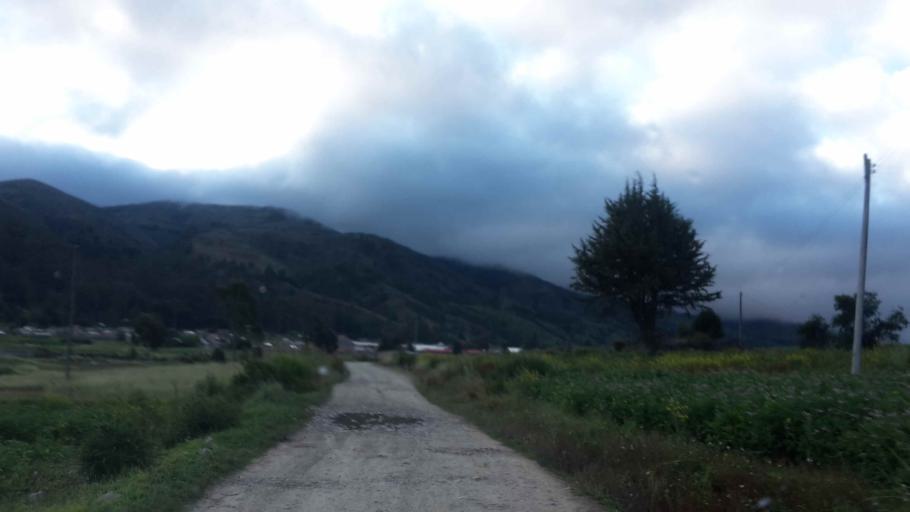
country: BO
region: Cochabamba
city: Colomi
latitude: -17.2764
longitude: -65.9167
